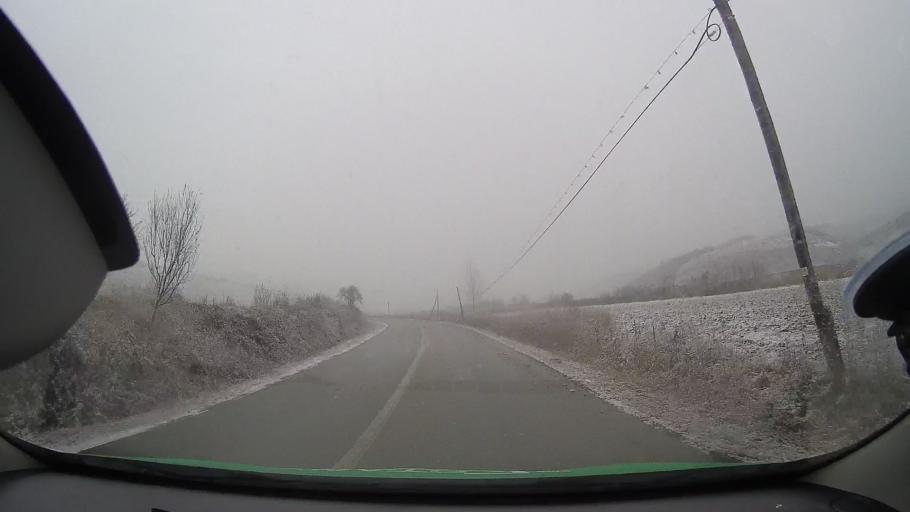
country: RO
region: Alba
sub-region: Comuna Lopadea Noua
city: Lopadea Noua
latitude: 46.2941
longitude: 23.8416
